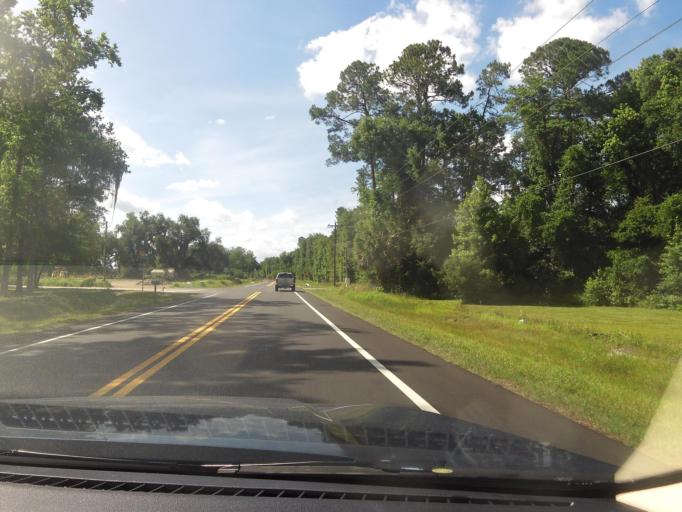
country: US
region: Florida
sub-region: Nassau County
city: Callahan
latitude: 30.5969
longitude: -81.8628
